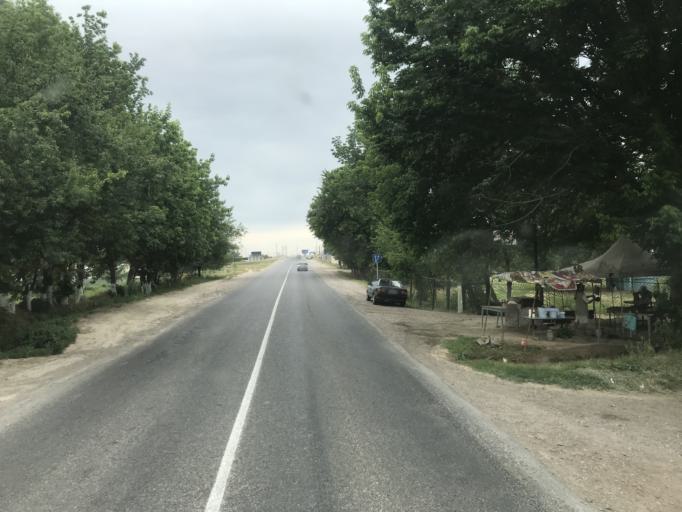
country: UZ
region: Toshkent
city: Yangiyul
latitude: 41.3297
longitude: 68.9025
